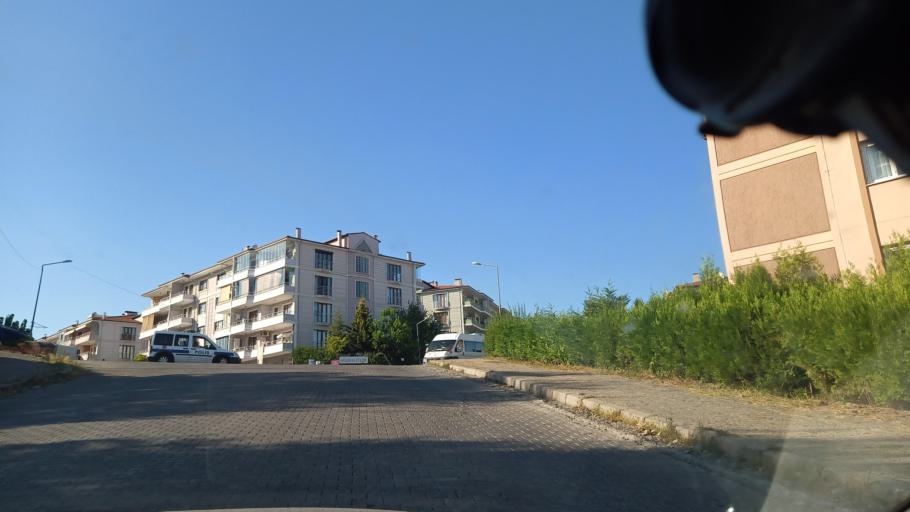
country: TR
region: Sakarya
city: Kazimpasa
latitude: 40.8599
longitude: 30.2922
